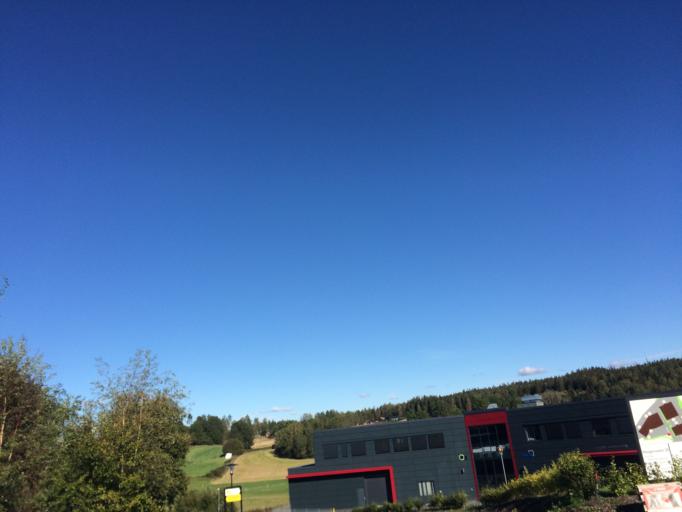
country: NO
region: Akershus
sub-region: Ski
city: Ski
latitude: 59.7220
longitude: 10.7913
